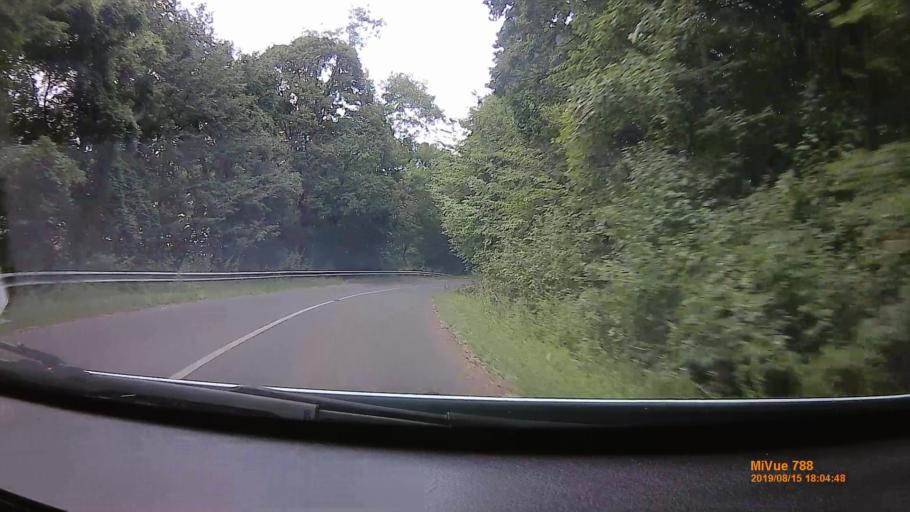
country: HU
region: Borsod-Abauj-Zemplen
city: Sajobabony
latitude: 48.1517
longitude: 20.6717
